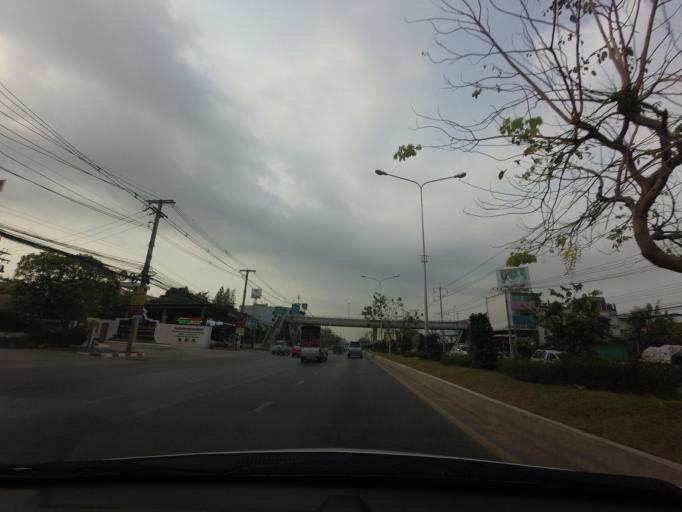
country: TH
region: Bangkok
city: Thawi Watthana
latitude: 13.7631
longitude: 100.3286
